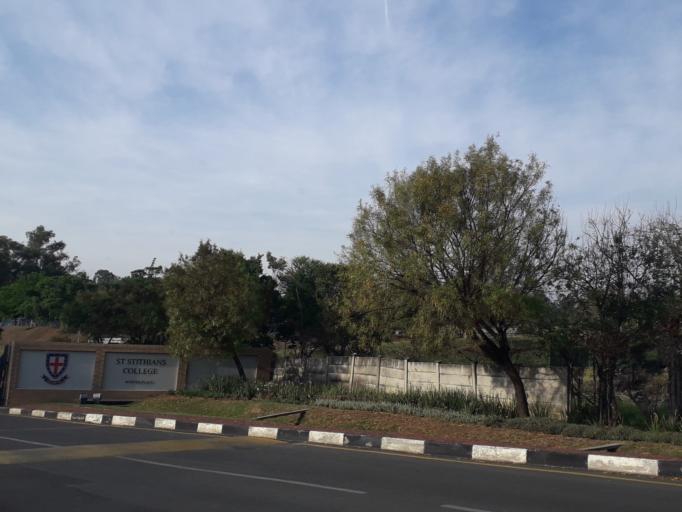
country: ZA
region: Gauteng
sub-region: City of Johannesburg Metropolitan Municipality
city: Johannesburg
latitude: -26.0822
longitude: 28.0181
